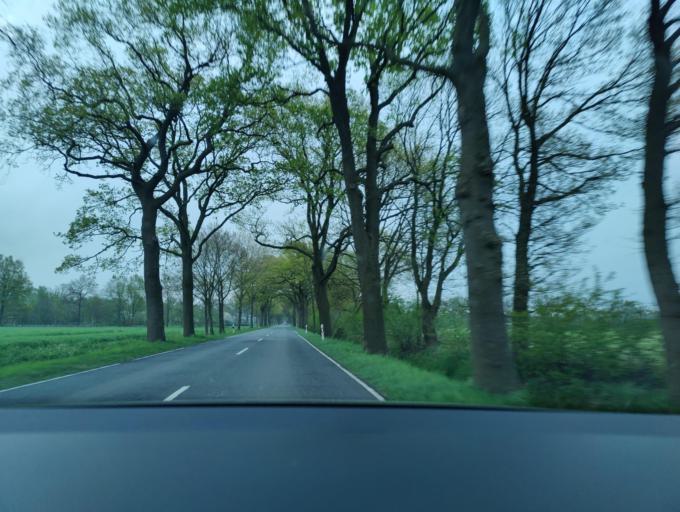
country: DE
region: Lower Saxony
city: Wietmarschen
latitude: 52.5054
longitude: 7.1730
